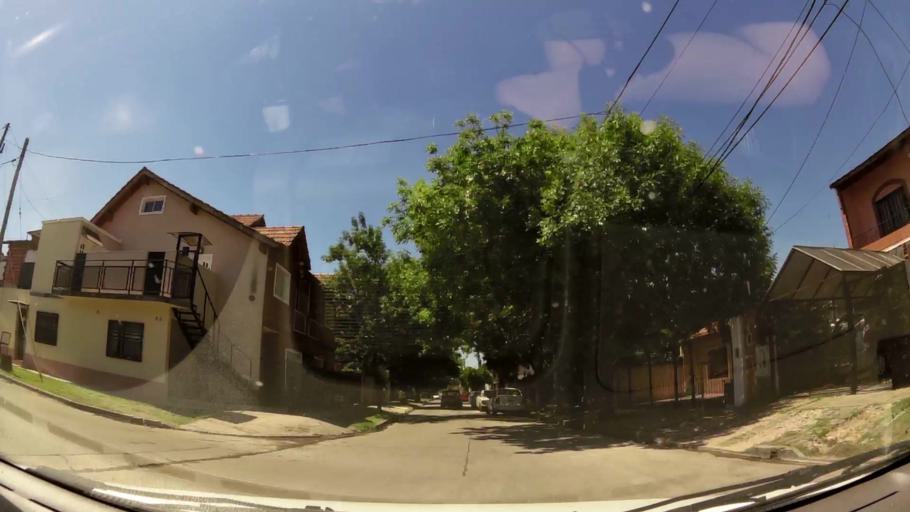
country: AR
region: Buenos Aires
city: Ituzaingo
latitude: -34.6604
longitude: -58.6853
